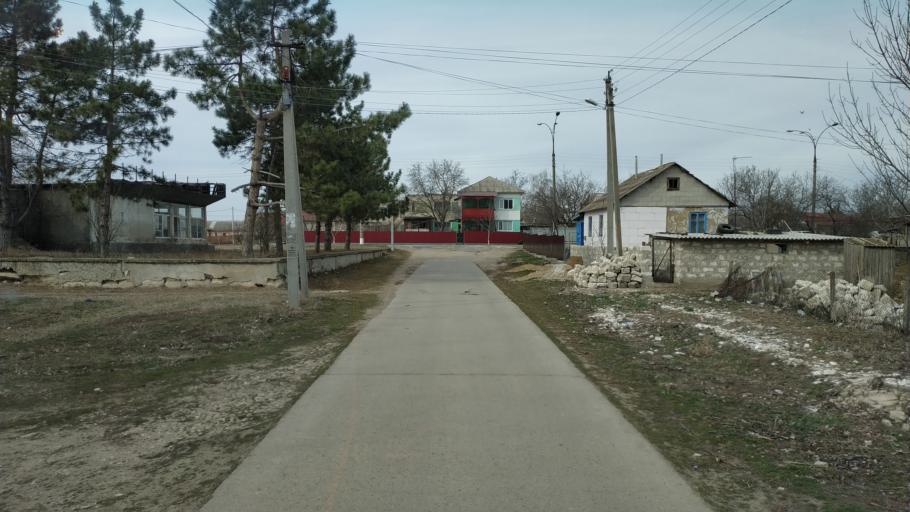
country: MD
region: Hincesti
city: Dancu
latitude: 46.8586
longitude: 28.2505
